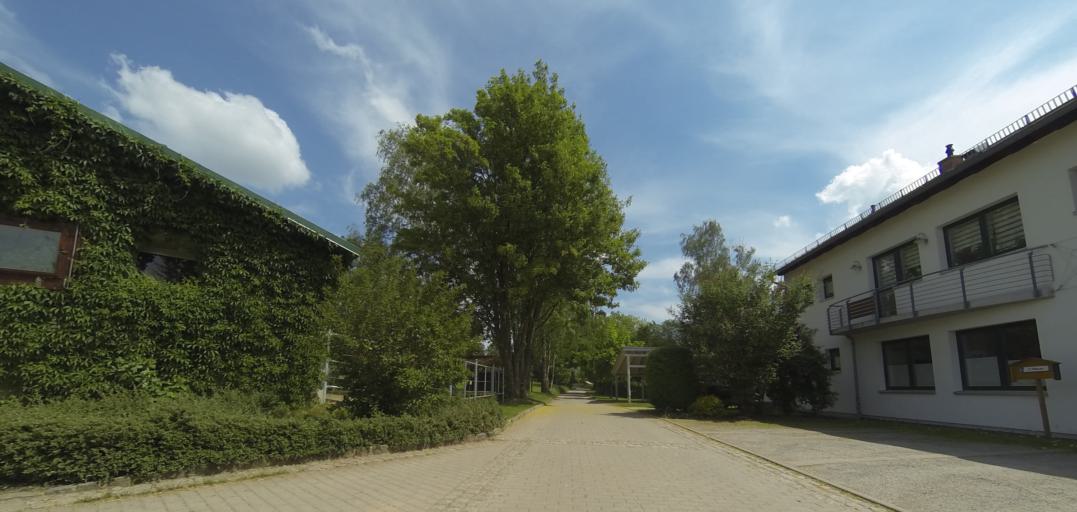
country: DE
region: Saxony
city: Grossharthau
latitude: 51.1074
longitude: 14.1095
